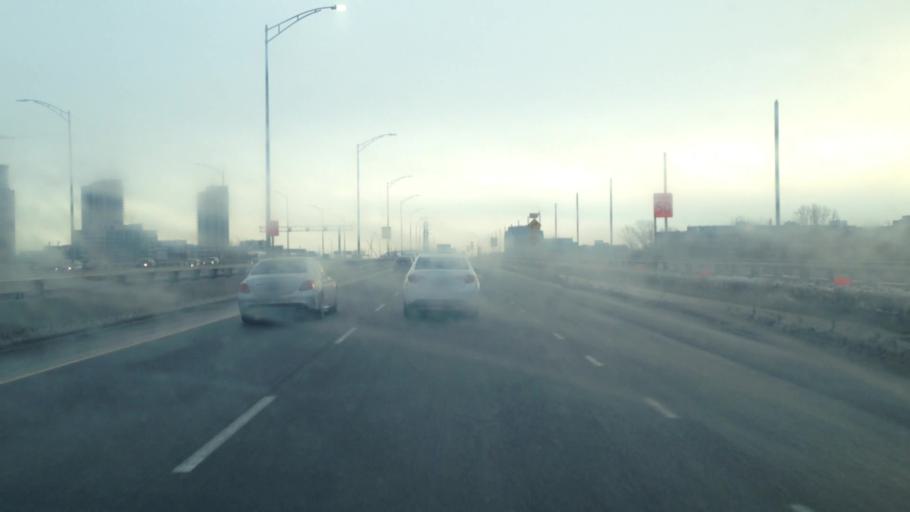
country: CA
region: Quebec
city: Westmount
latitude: 45.4711
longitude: -73.5546
